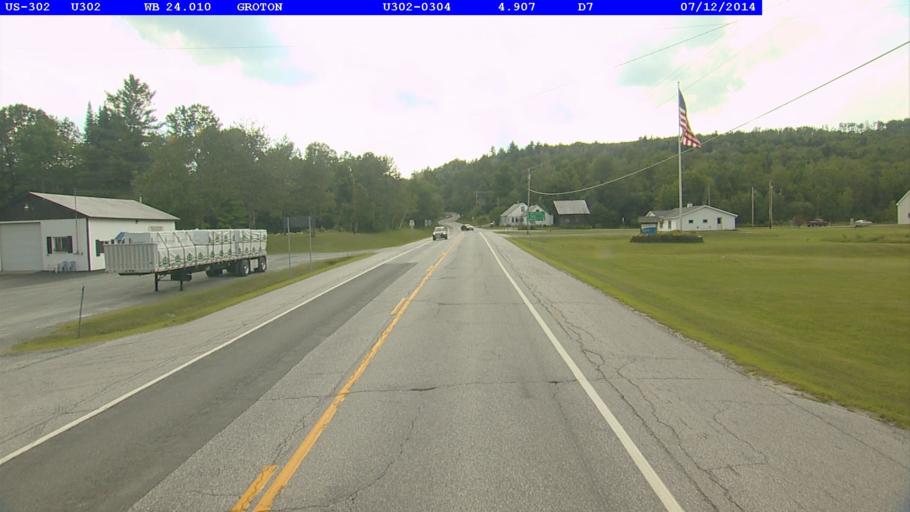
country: US
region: New Hampshire
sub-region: Grafton County
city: Woodsville
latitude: 44.2195
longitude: -72.2240
